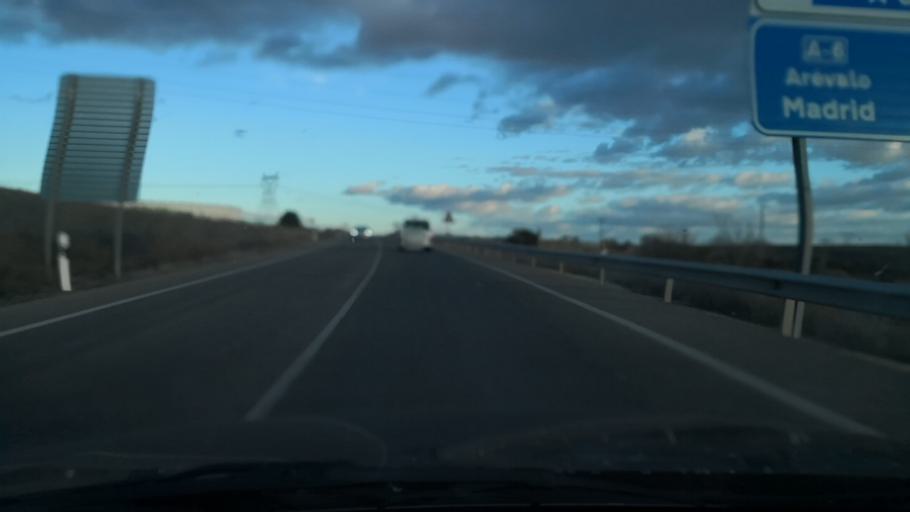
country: ES
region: Castille and Leon
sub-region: Provincia de Valladolid
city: Medina del Campo
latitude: 41.3111
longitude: -4.9011
